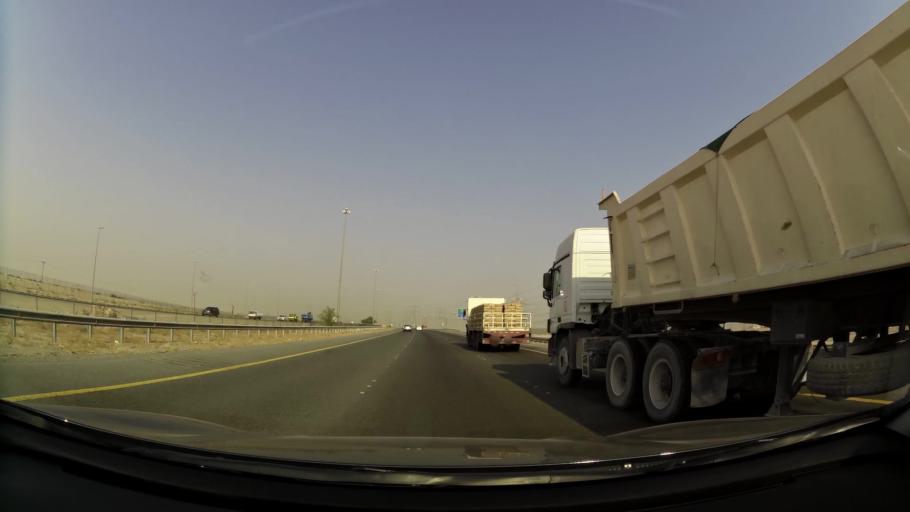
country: KW
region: Al Asimah
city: Ar Rabiyah
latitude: 29.2436
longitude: 47.8777
